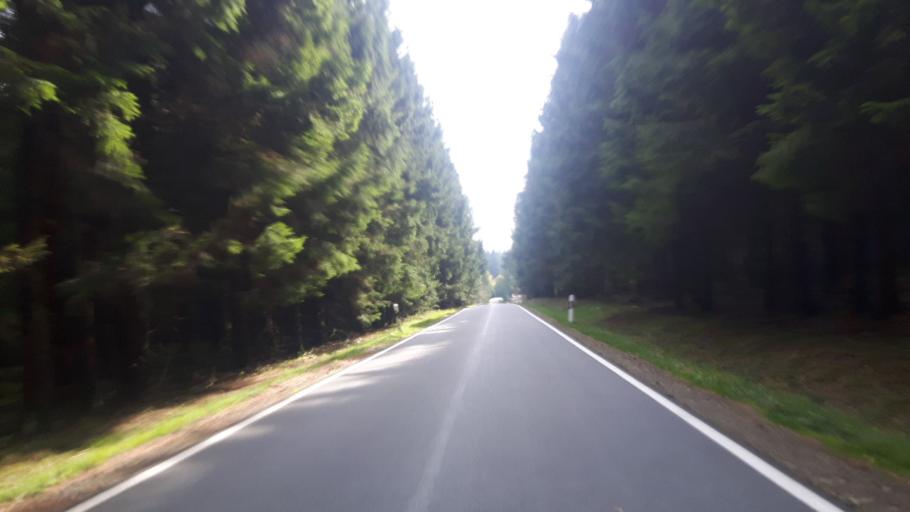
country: DE
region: North Rhine-Westphalia
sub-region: Regierungsbezirk Arnsberg
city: Erndtebruck
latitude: 50.9008
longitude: 8.2434
